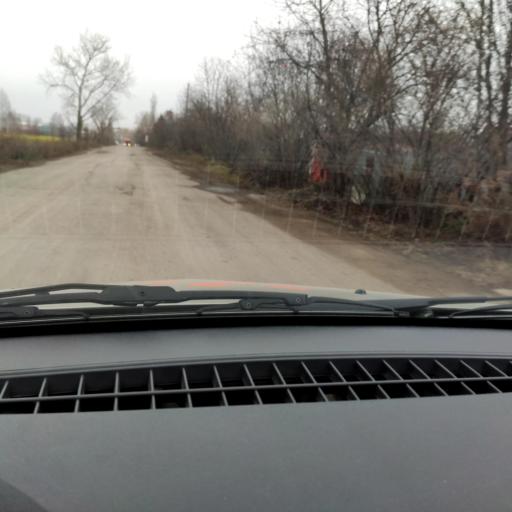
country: RU
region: Bashkortostan
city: Ufa
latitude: 54.5795
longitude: 55.8898
